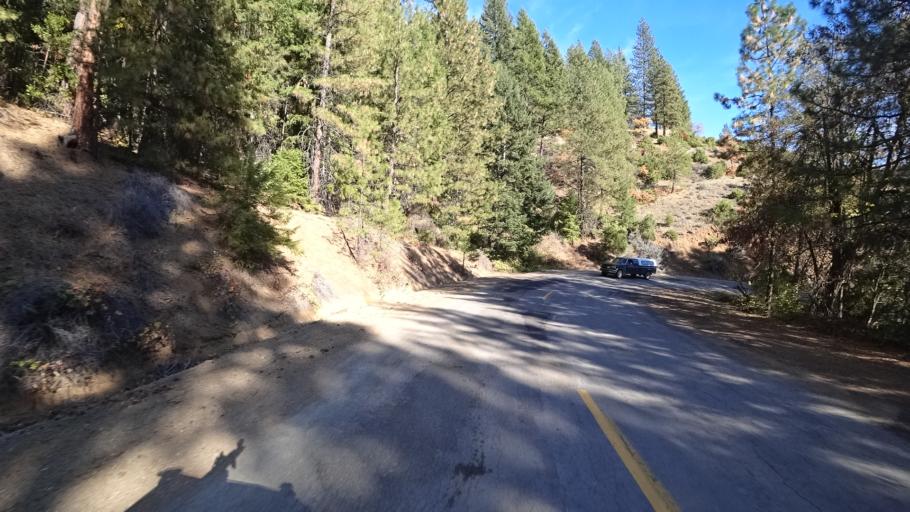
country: US
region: California
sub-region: Siskiyou County
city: Yreka
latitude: 41.7311
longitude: -122.7231
